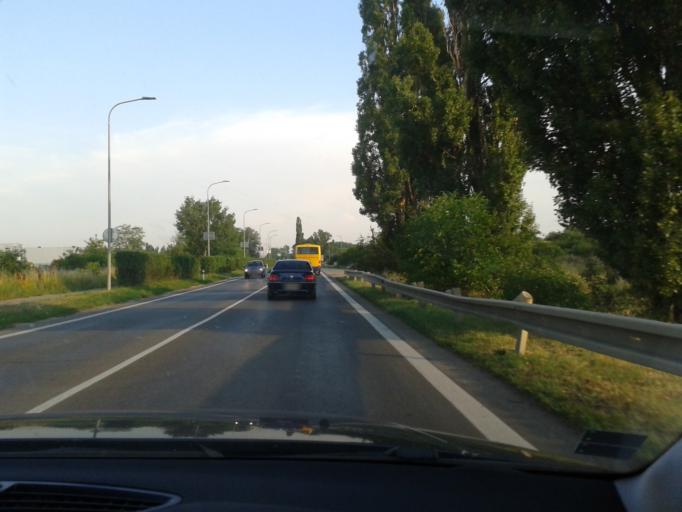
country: SK
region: Trnavsky
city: Hlohovec
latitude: 48.4326
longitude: 17.7869
